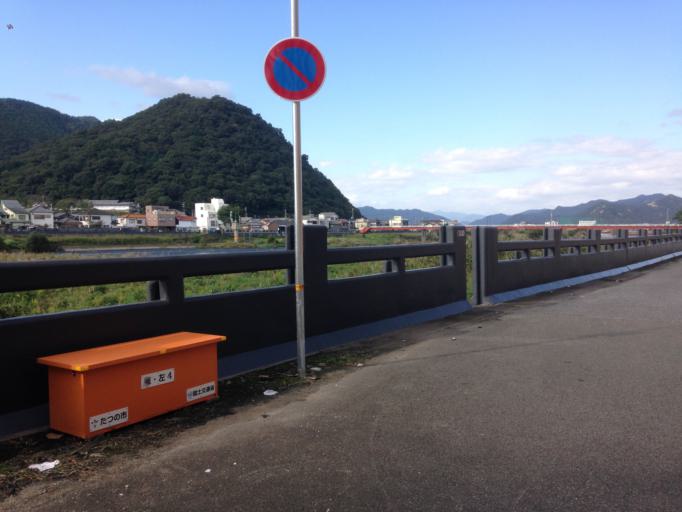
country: JP
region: Hyogo
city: Tatsunocho-tominaga
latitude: 34.8642
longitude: 134.5494
